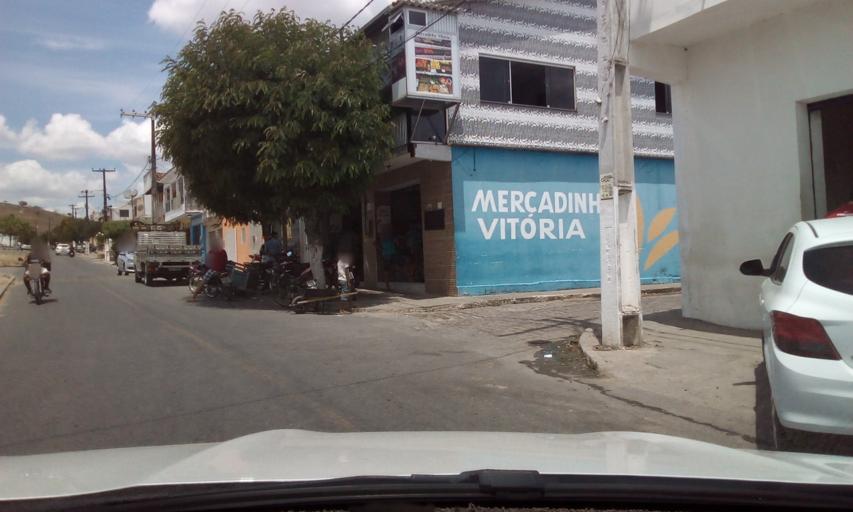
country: BR
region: Paraiba
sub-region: Gurinhem
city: Gurinhem
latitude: -7.1251
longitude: -35.4238
